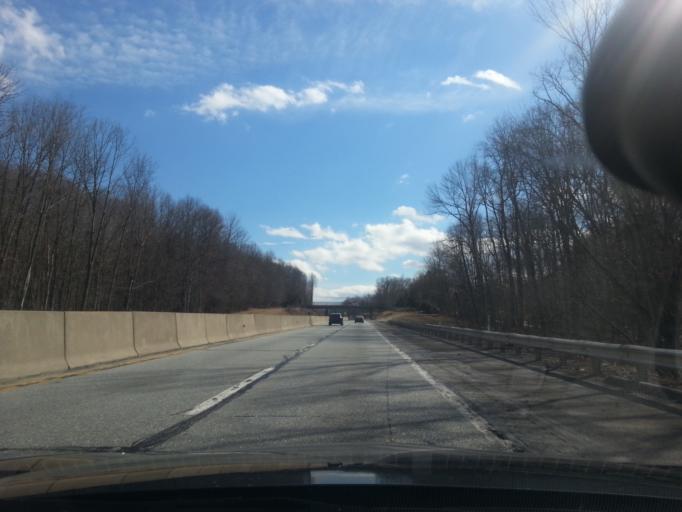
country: US
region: Pennsylvania
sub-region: Bucks County
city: Spinnerstown
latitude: 40.3882
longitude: -75.4102
